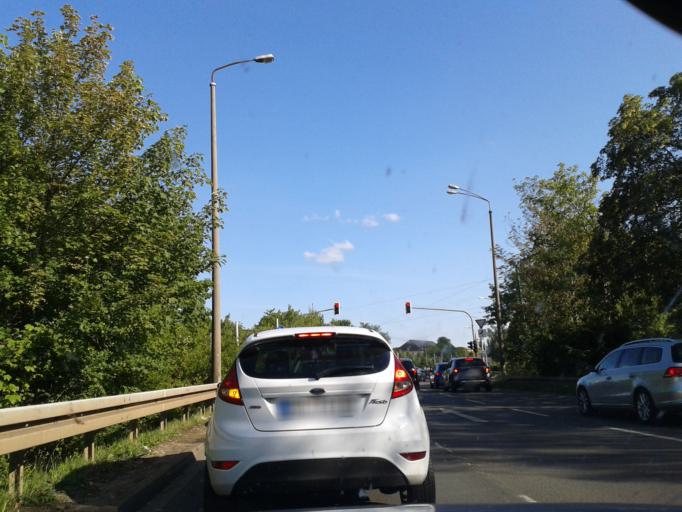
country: DE
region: Saxony-Anhalt
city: Halle (Saale)
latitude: 51.4989
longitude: 11.9798
